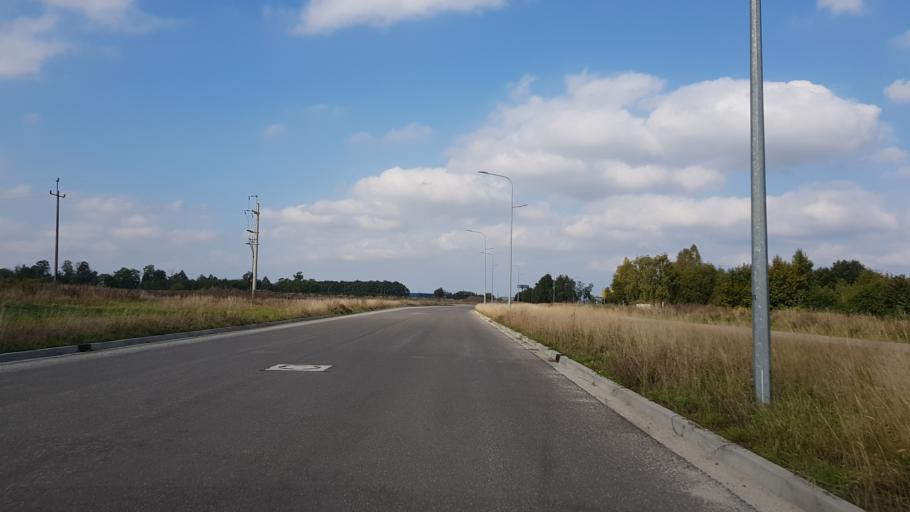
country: PL
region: West Pomeranian Voivodeship
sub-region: Koszalin
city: Koszalin
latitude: 54.1781
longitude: 16.1553
